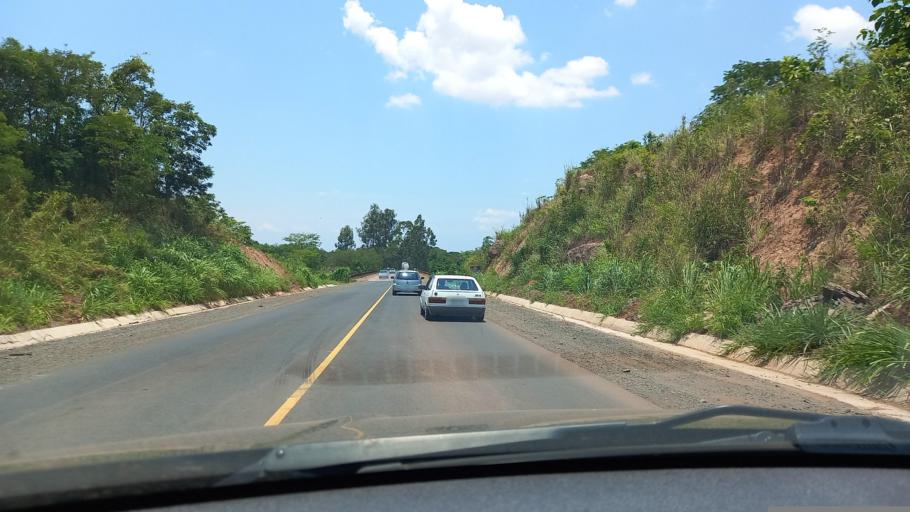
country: BR
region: Sao Paulo
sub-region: Moji-Guacu
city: Mogi-Gaucu
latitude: -22.3746
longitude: -46.8748
